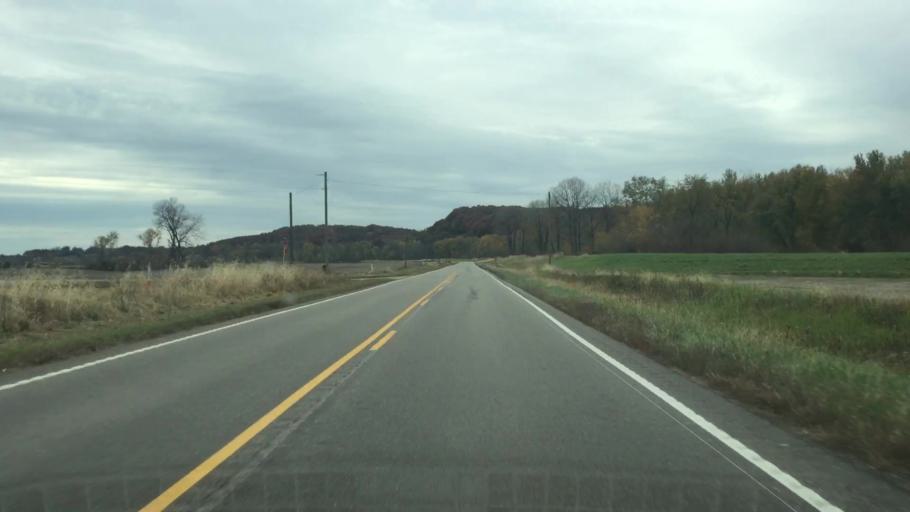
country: US
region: Missouri
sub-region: Callaway County
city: Fulton
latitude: 38.7054
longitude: -91.7769
